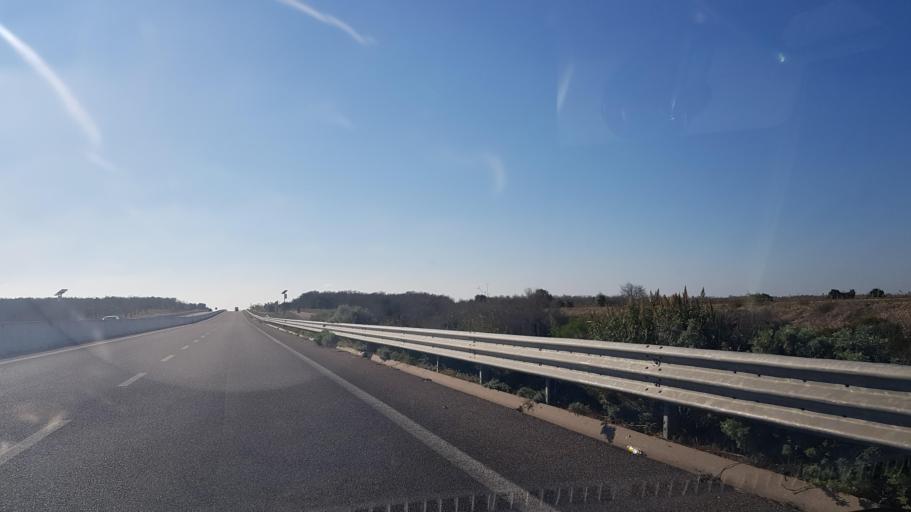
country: IT
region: Apulia
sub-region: Provincia di Lecce
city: Giurdignano
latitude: 40.1436
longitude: 18.4459
